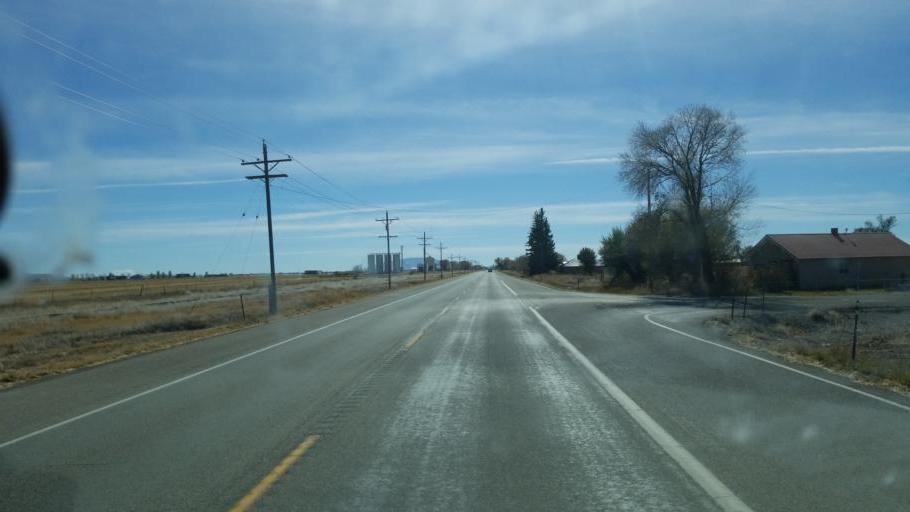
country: US
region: Colorado
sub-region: Conejos County
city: Conejos
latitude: 37.2329
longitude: -105.9723
